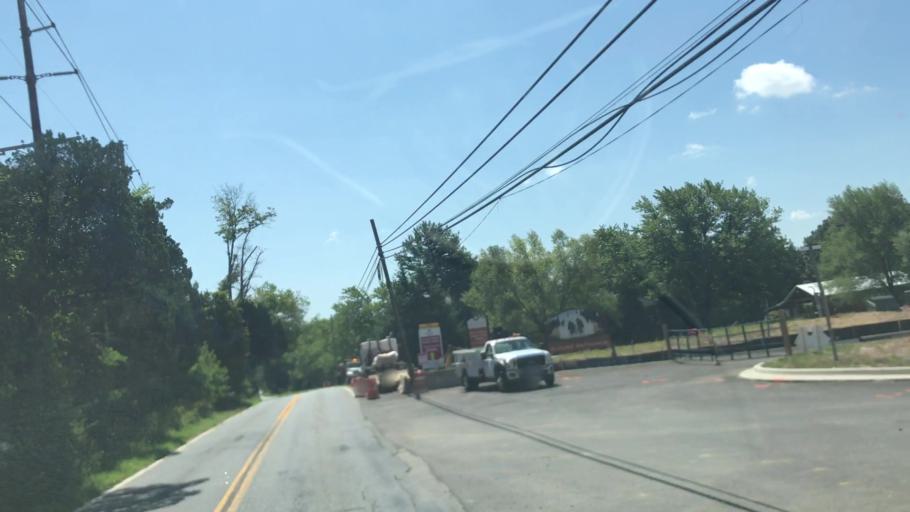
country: US
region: Maryland
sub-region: Prince George's County
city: Brandywine
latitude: 38.7169
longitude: -76.8894
